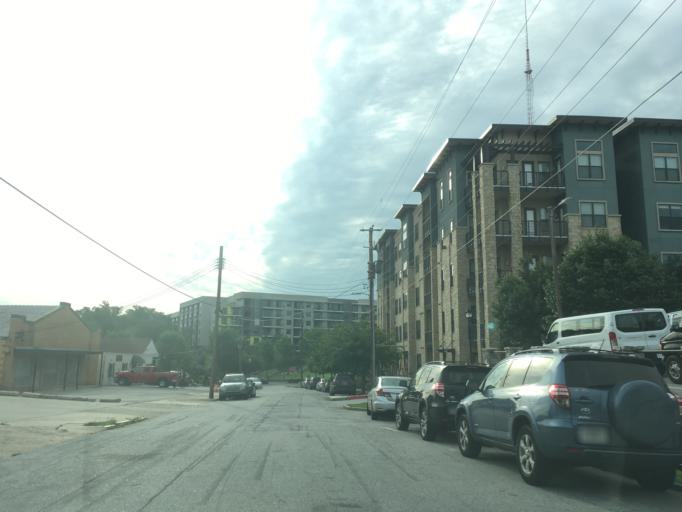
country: US
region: Georgia
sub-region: Fulton County
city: Atlanta
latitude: 33.7661
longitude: -84.3667
